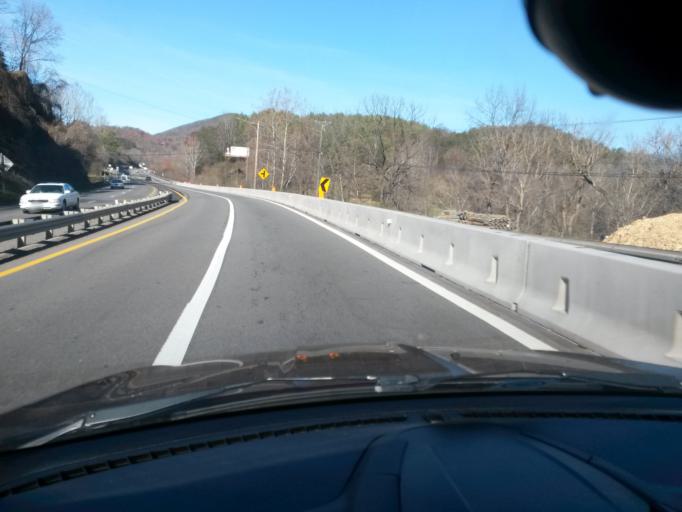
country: US
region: Virginia
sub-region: Roanoke County
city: Narrows
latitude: 37.1803
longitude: -79.9351
